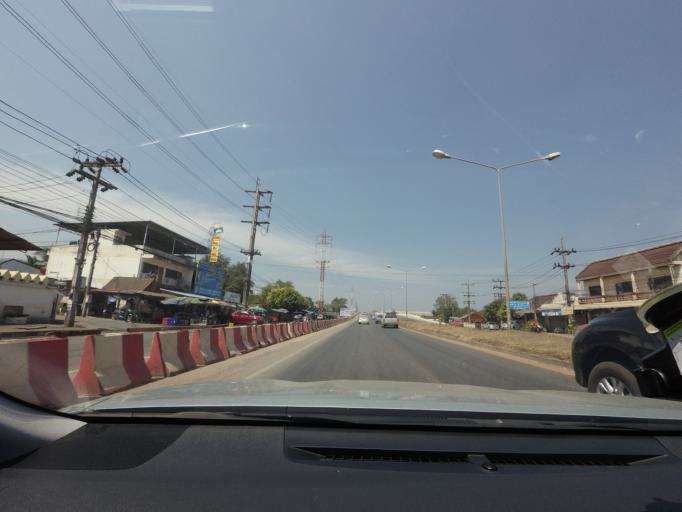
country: TH
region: Surat Thani
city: Surat Thani
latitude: 9.1484
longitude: 99.3894
